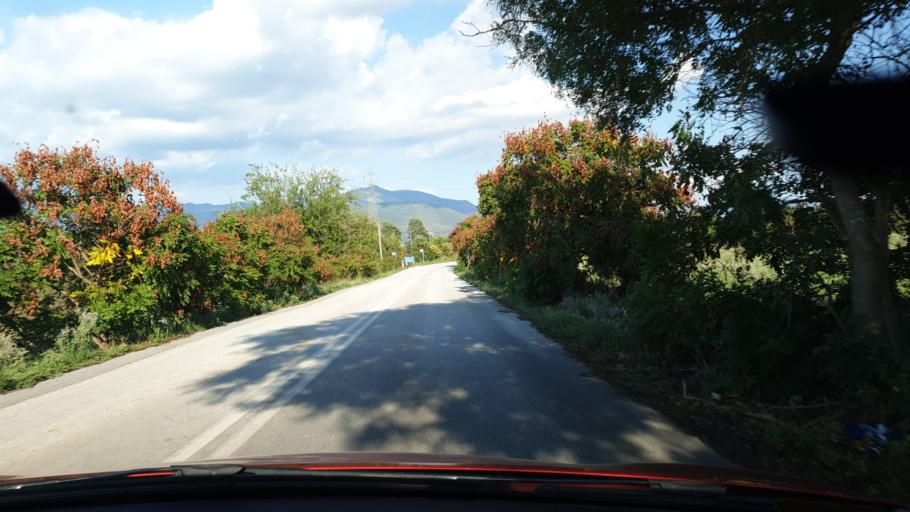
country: GR
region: Central Macedonia
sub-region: Nomos Thessalonikis
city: Souroti
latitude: 40.4756
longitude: 23.0987
